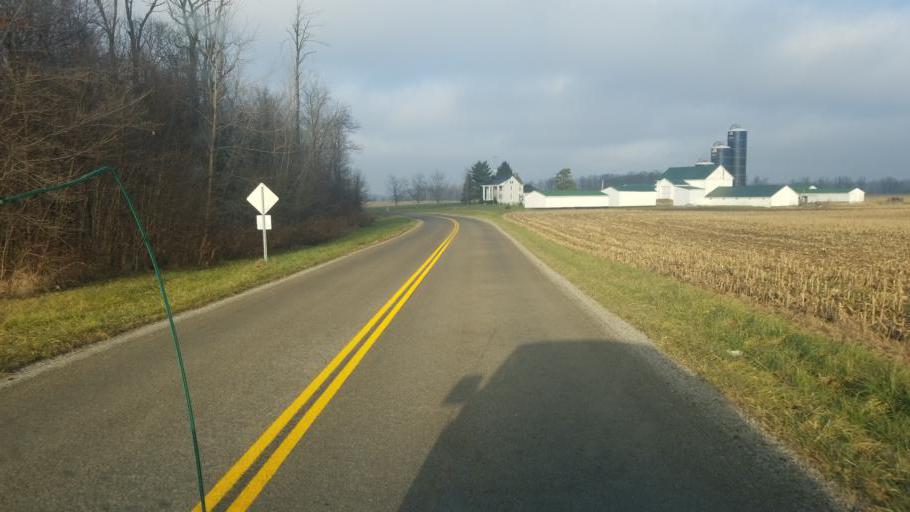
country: US
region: Ohio
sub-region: Hardin County
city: Kenton
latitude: 40.6857
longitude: -83.5749
